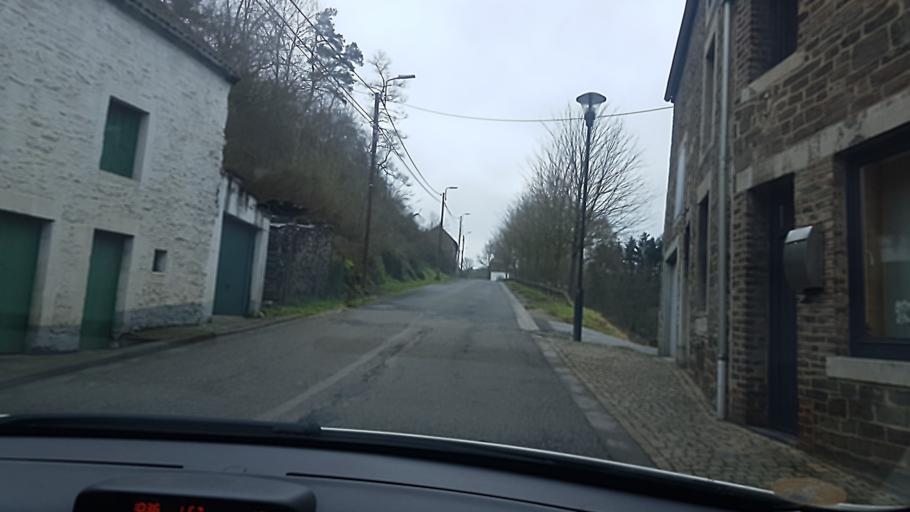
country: BE
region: Wallonia
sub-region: Province de Namur
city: Couvin
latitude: 50.0704
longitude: 4.6075
